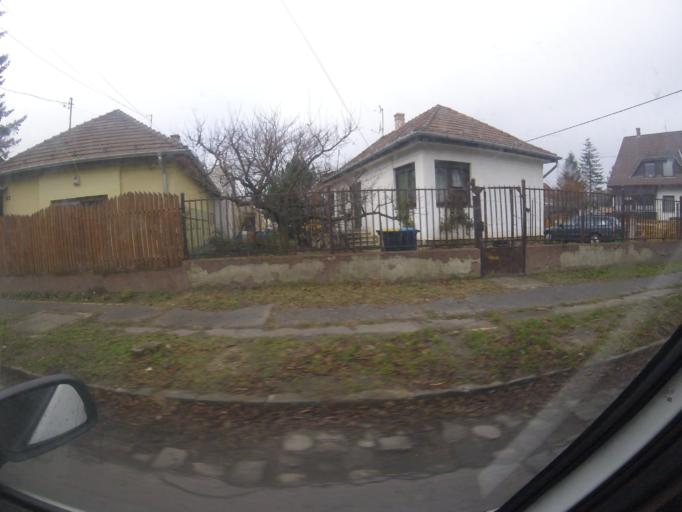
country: HU
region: Pest
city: Budakalasz
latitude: 47.5814
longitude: 19.0544
